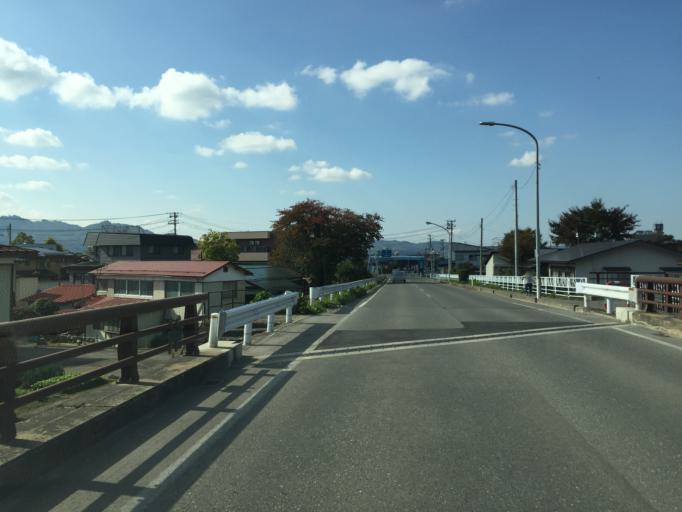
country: JP
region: Yamagata
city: Yonezawa
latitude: 37.9048
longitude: 140.1298
